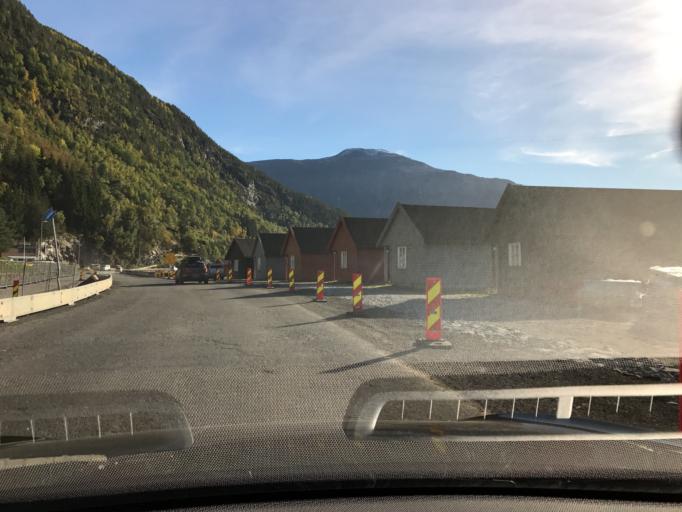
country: NO
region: Sogn og Fjordane
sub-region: Sogndal
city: Sogndalsfjora
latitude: 61.2301
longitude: 7.1238
